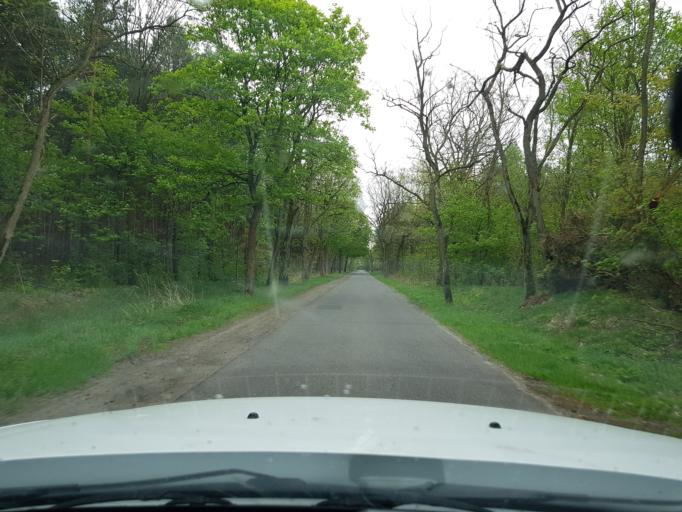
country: PL
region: West Pomeranian Voivodeship
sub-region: Powiat mysliborski
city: Debno
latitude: 52.7022
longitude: 14.6534
